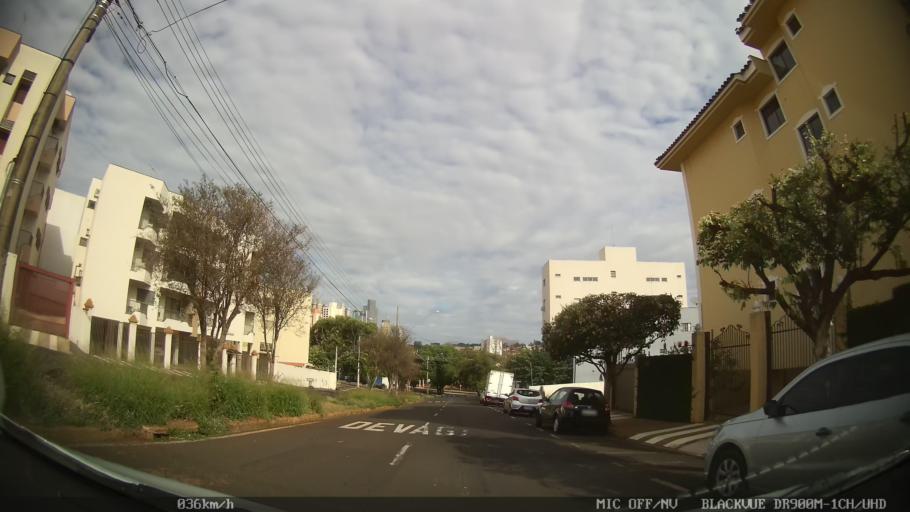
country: BR
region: Sao Paulo
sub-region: Sao Jose Do Rio Preto
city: Sao Jose do Rio Preto
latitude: -20.8281
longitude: -49.4030
